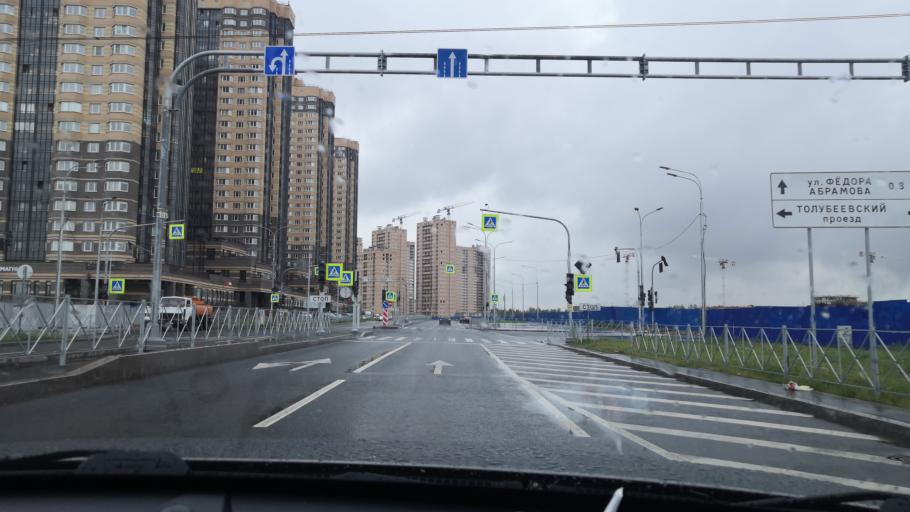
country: RU
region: Leningrad
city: Parnas
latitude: 60.0828
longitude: 30.3561
